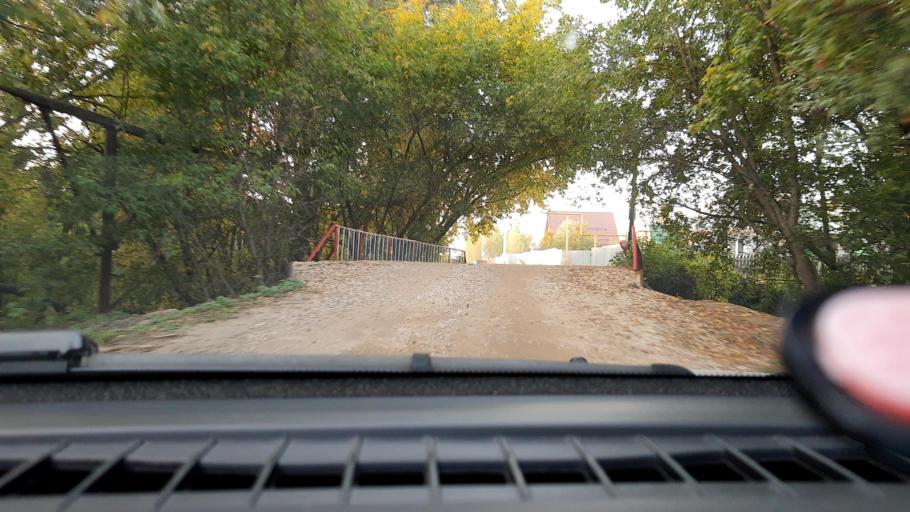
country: RU
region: Nizjnij Novgorod
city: Bor
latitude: 56.4029
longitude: 44.0358
